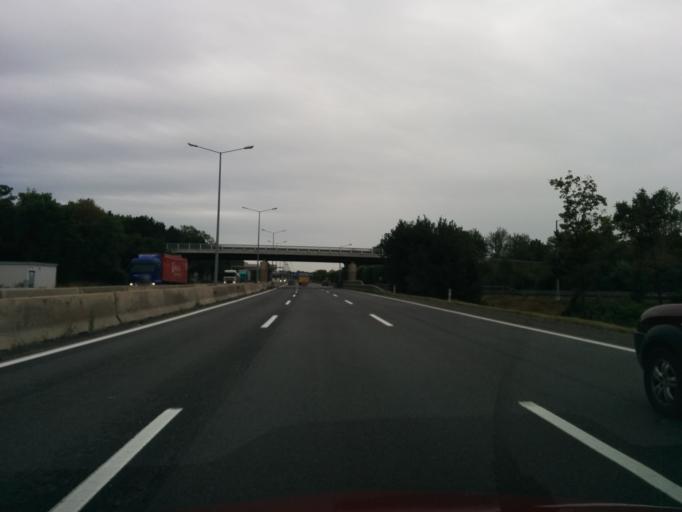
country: AT
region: Lower Austria
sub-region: Politischer Bezirk Modling
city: Brunn am Gebirge
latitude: 48.1175
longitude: 16.2983
